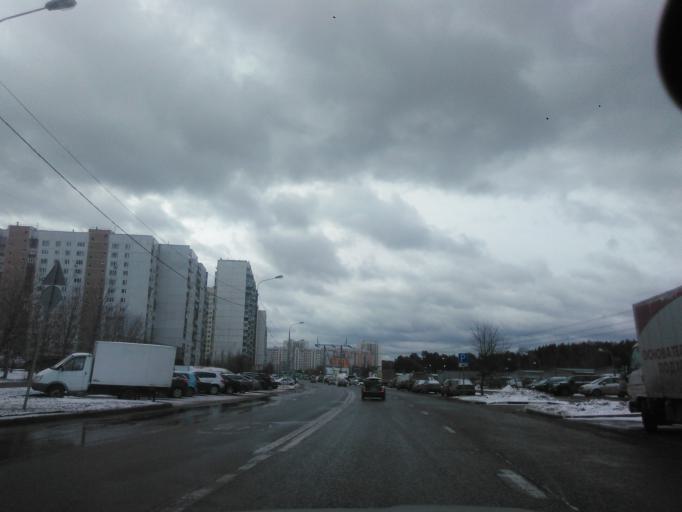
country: RU
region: Moskovskaya
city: Krasnogorsk
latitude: 55.8563
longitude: 37.3424
